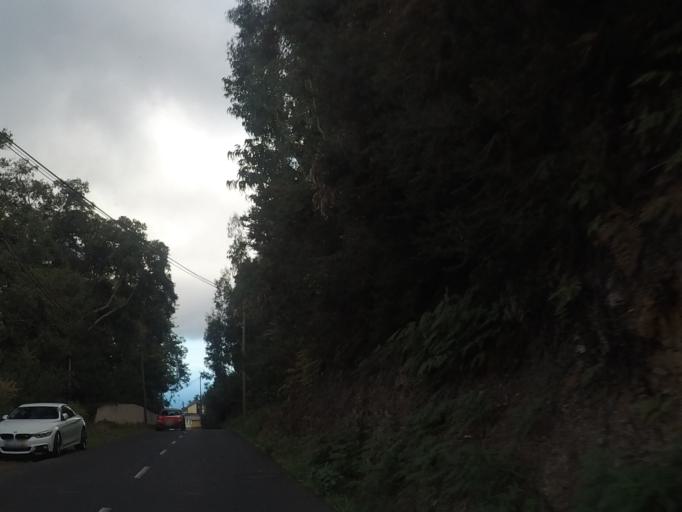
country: PT
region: Madeira
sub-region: Santa Cruz
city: Camacha
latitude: 32.6794
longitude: -16.8535
